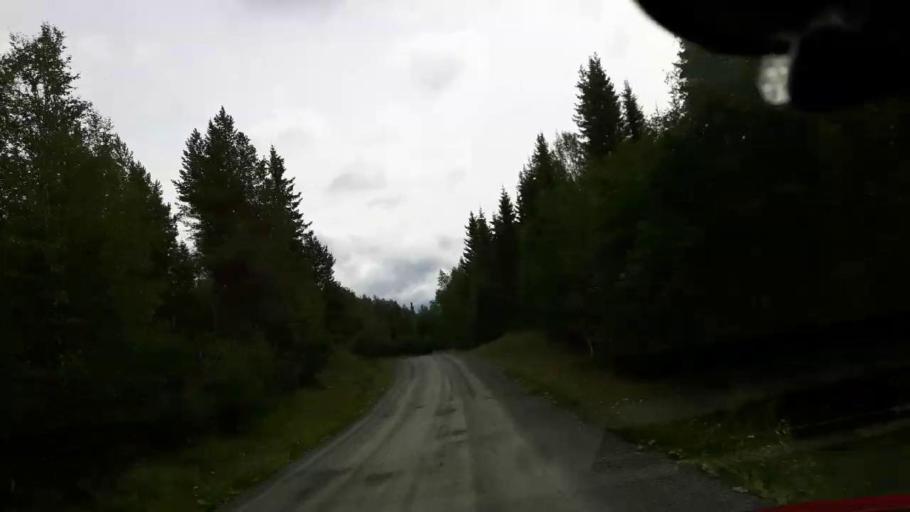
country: SE
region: Jaemtland
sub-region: Krokoms Kommun
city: Valla
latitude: 63.6666
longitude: 13.9638
